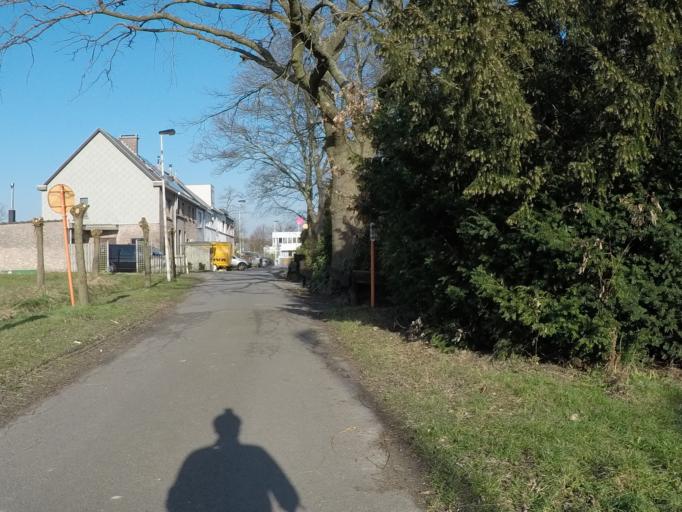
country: BE
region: Flanders
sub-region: Provincie Antwerpen
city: Edegem
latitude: 51.1513
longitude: 4.4329
